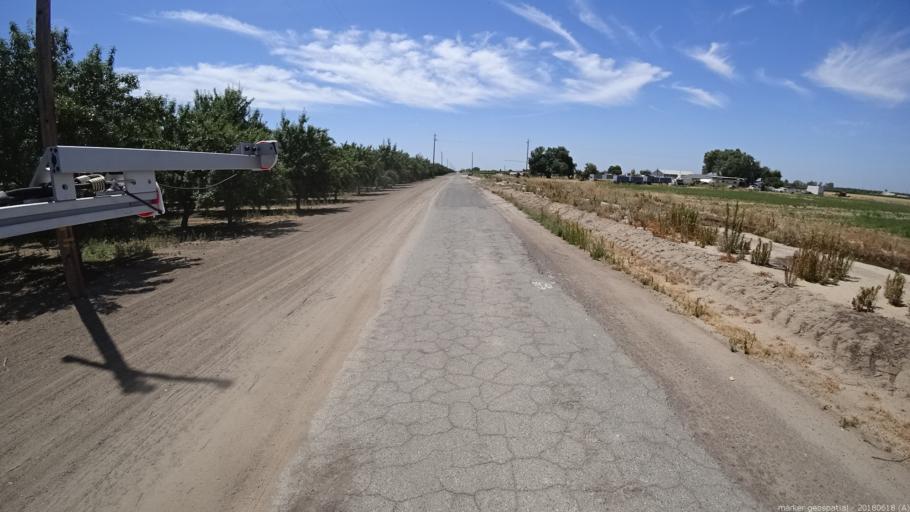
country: US
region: California
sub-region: Madera County
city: Parkwood
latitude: 36.8911
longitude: -120.1014
